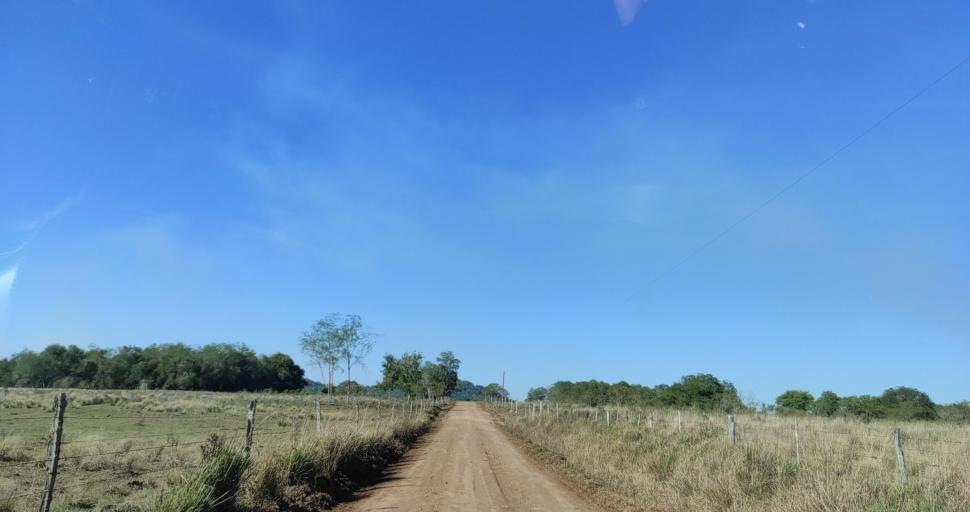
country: AR
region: Misiones
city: Cerro Cora
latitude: -27.6392
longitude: -55.6635
